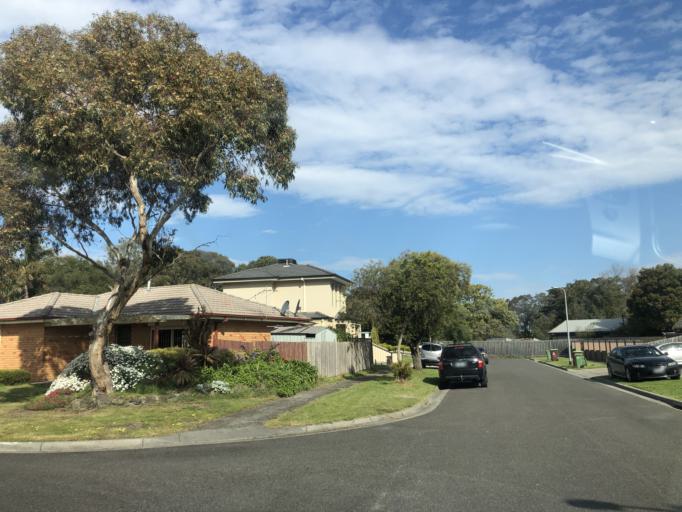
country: AU
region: Victoria
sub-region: Casey
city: Hampton Park
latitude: -38.0385
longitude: 145.2507
